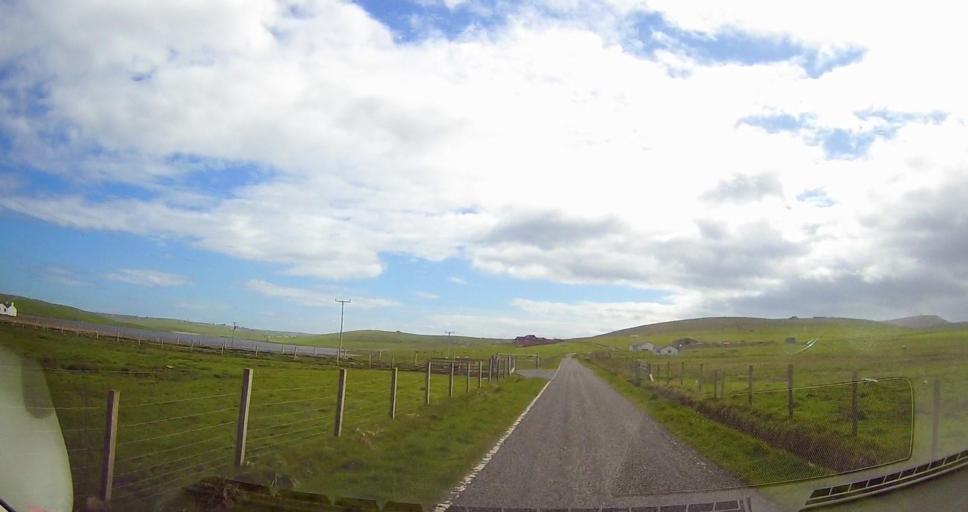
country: GB
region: Scotland
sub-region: Shetland Islands
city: Sandwick
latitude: 59.9366
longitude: -1.3459
